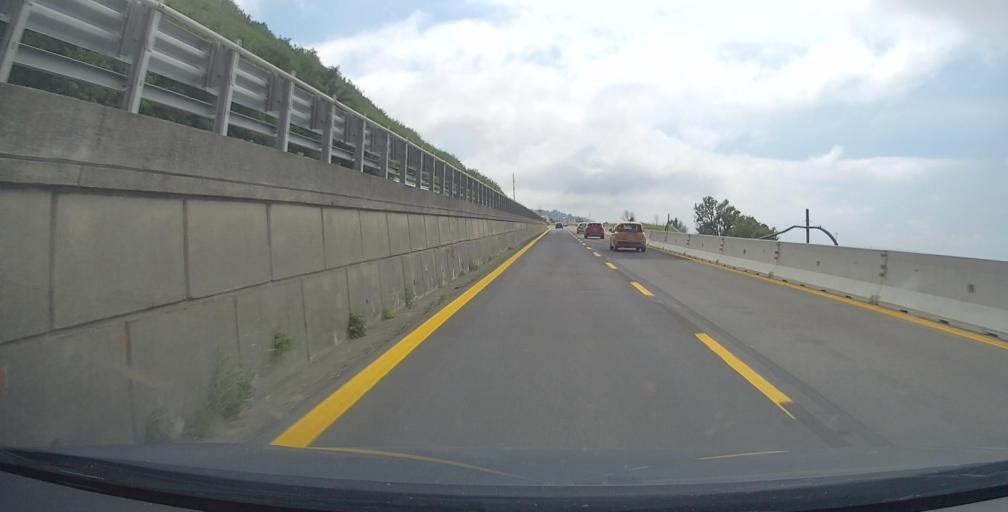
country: IT
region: Calabria
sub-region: Provincia di Vibo-Valentia
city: Maierato
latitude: 38.7208
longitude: 16.1576
